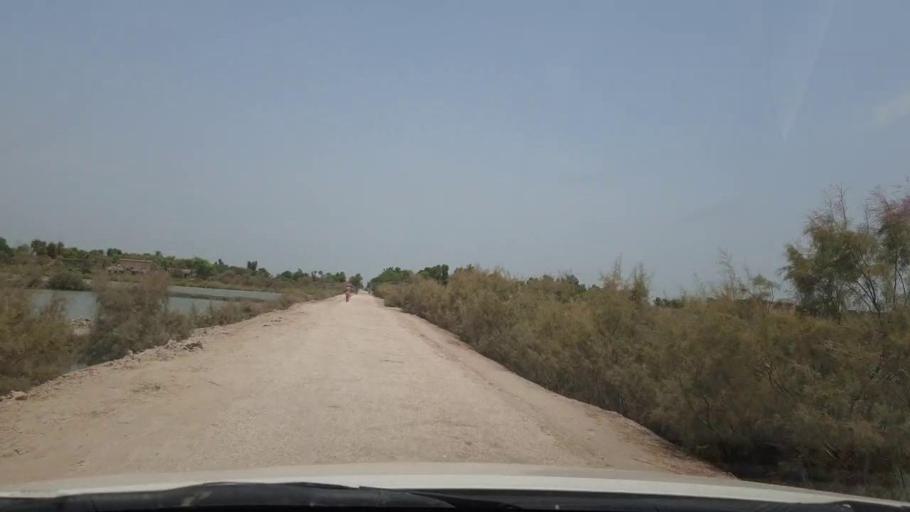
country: PK
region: Sindh
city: Rustam jo Goth
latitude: 28.0294
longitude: 68.8134
